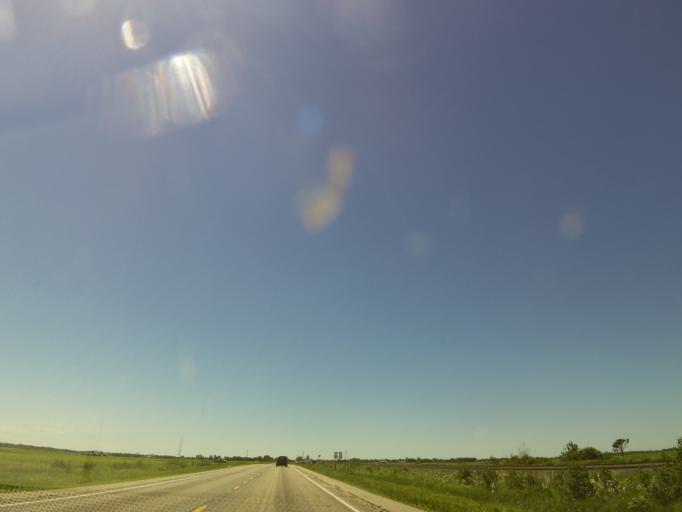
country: US
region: Minnesota
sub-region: Mahnomen County
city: Mahnomen
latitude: 47.3430
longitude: -95.9673
